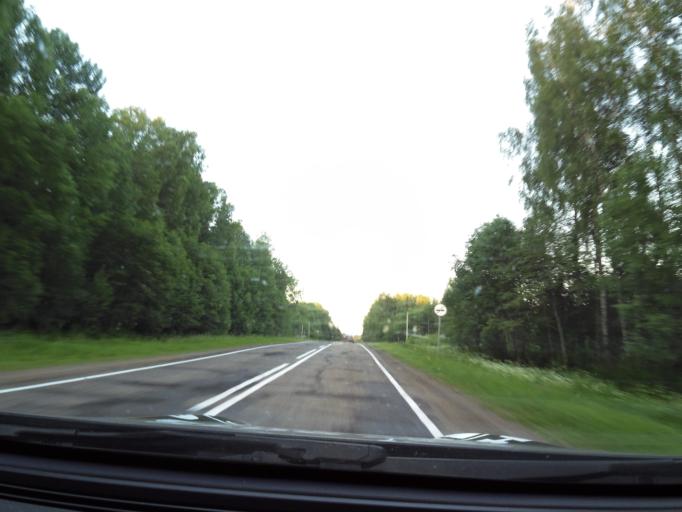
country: RU
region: Jaroslavl
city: Lyubim
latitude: 58.3593
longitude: 40.5307
